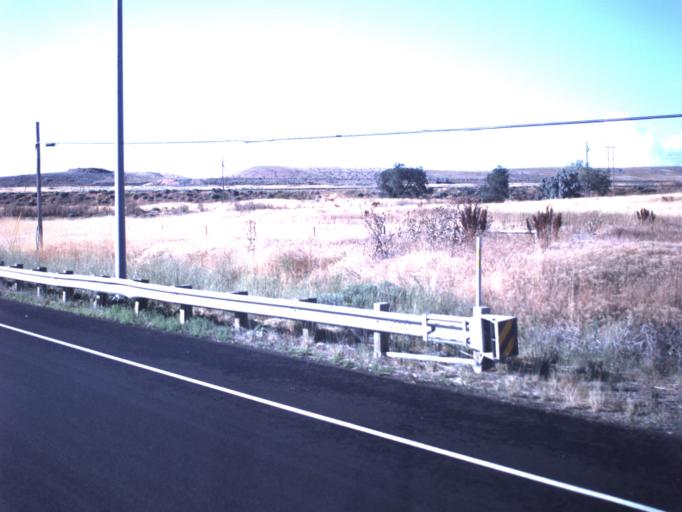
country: US
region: Utah
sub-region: Salt Lake County
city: Oquirrh
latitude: 40.6549
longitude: -112.0771
